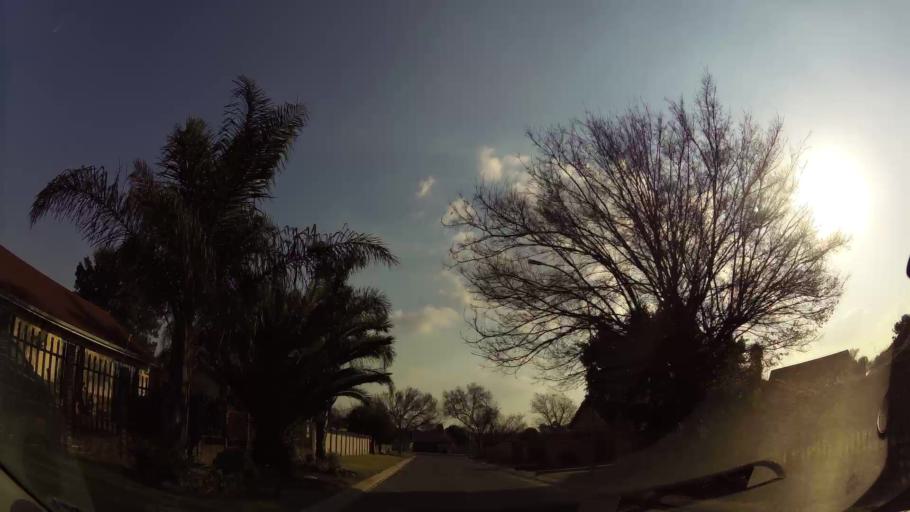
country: ZA
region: Gauteng
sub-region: Ekurhuleni Metropolitan Municipality
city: Benoni
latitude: -26.1351
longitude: 28.3648
